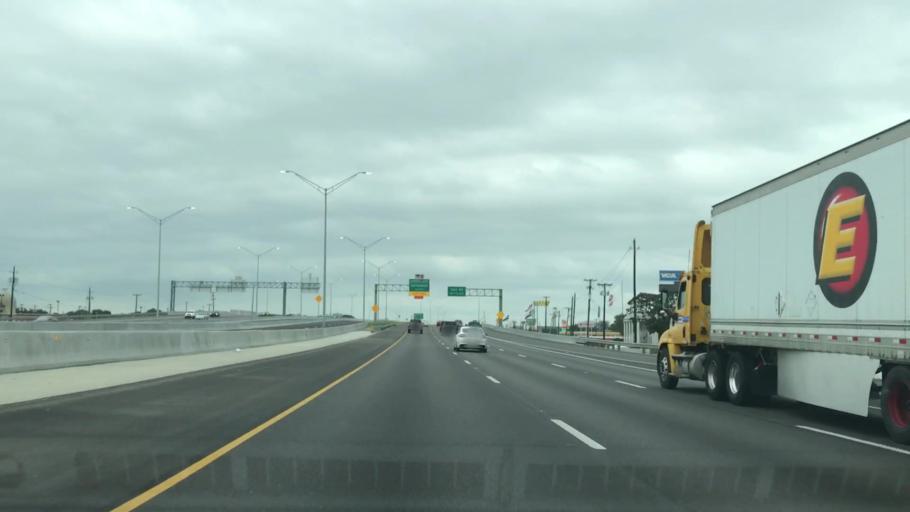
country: US
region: Texas
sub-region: Dallas County
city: Irving
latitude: 32.8367
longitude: -96.9550
